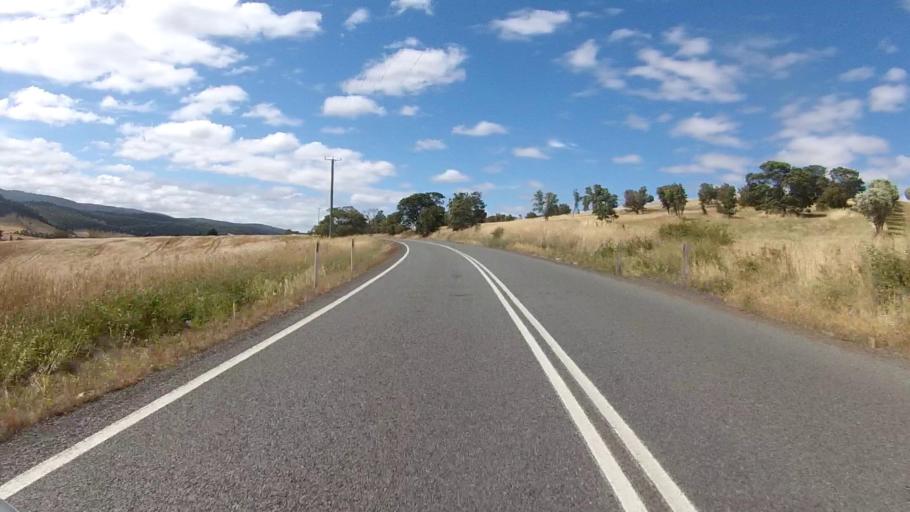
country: AU
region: Tasmania
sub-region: Sorell
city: Sorell
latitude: -42.6049
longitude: 147.4180
